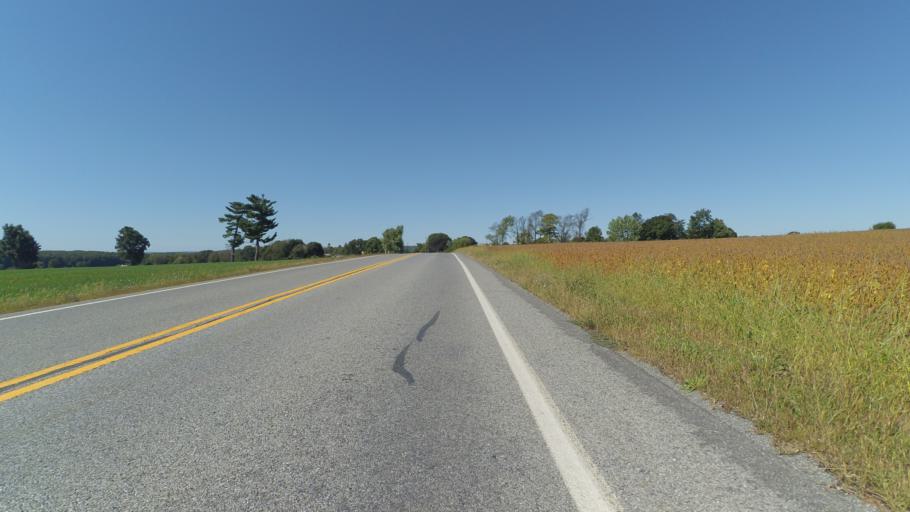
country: US
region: Pennsylvania
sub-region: Centre County
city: Pine Grove Mills
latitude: 40.7564
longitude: -77.9036
